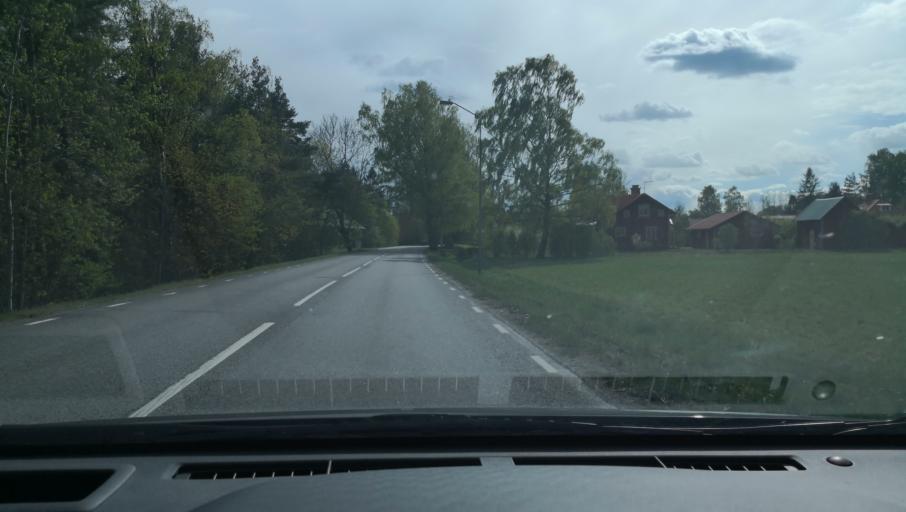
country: SE
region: OErebro
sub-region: Kumla Kommun
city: Kumla
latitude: 59.0824
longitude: 15.1563
